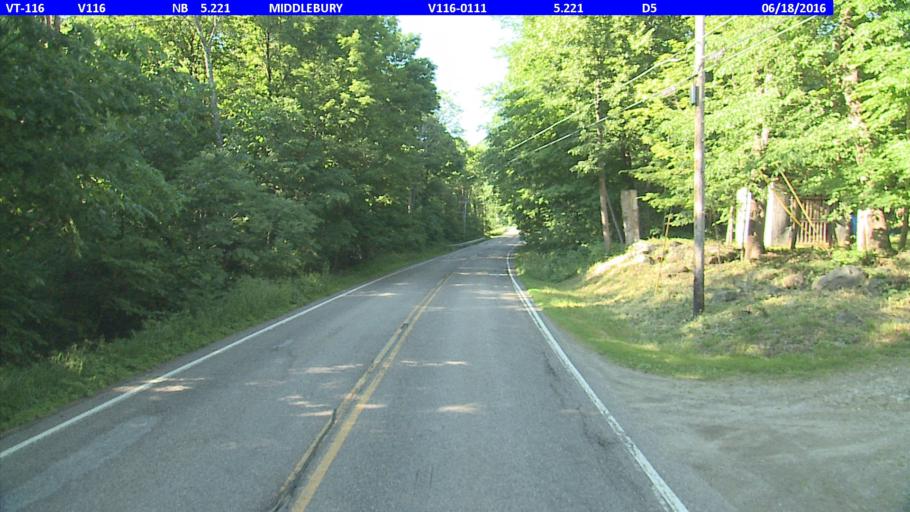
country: US
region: Vermont
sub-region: Addison County
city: Middlebury (village)
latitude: 44.0353
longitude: -73.0920
